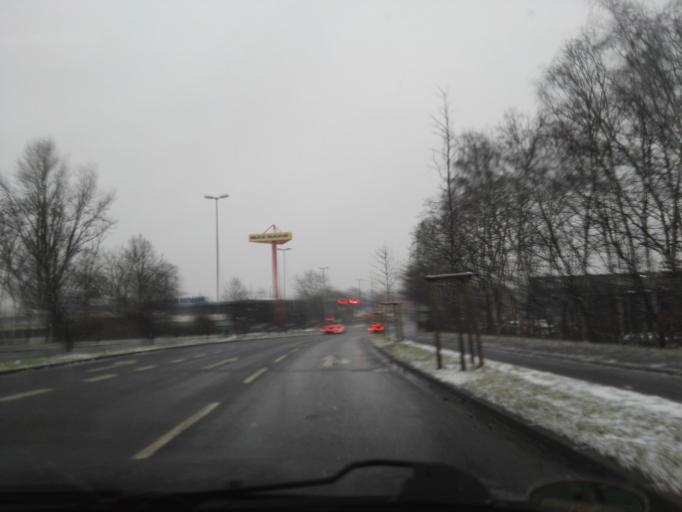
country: DE
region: Lower Saxony
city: Braunschweig
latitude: 52.2464
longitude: 10.5143
